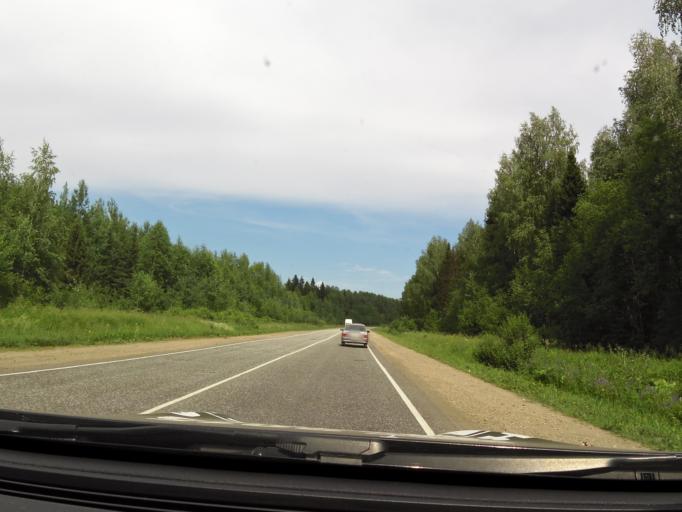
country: RU
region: Kirov
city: Vakhrushi
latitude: 58.6548
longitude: 49.8981
